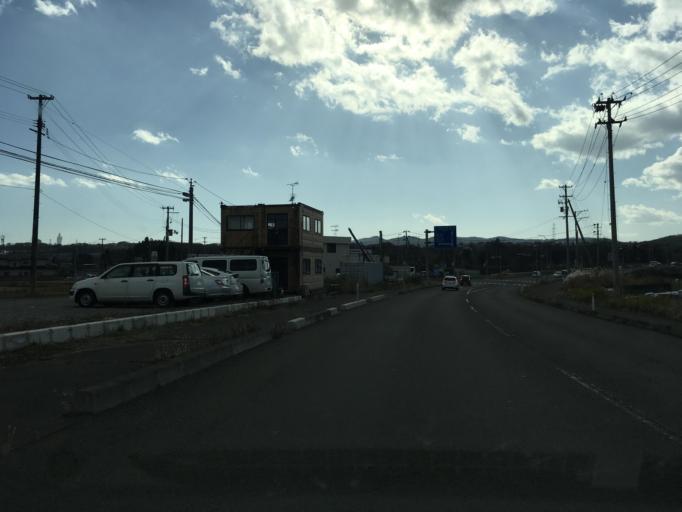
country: JP
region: Miyagi
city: Sendai-shi
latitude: 38.3318
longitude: 140.8017
